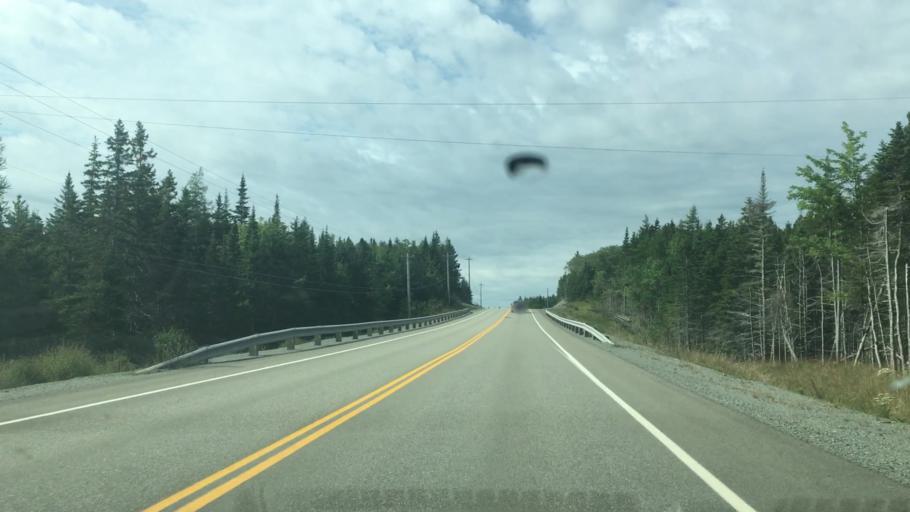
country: CA
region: Nova Scotia
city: Princeville
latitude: 45.6769
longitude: -60.7882
